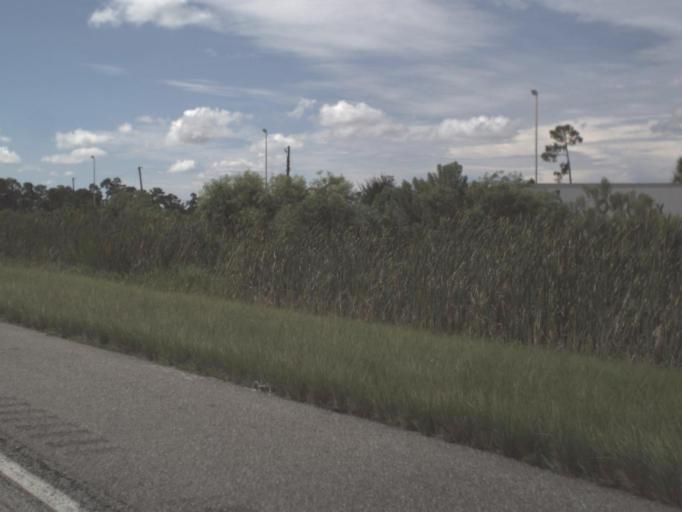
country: US
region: Florida
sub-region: Charlotte County
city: Harbour Heights
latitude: 27.0259
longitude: -82.0521
